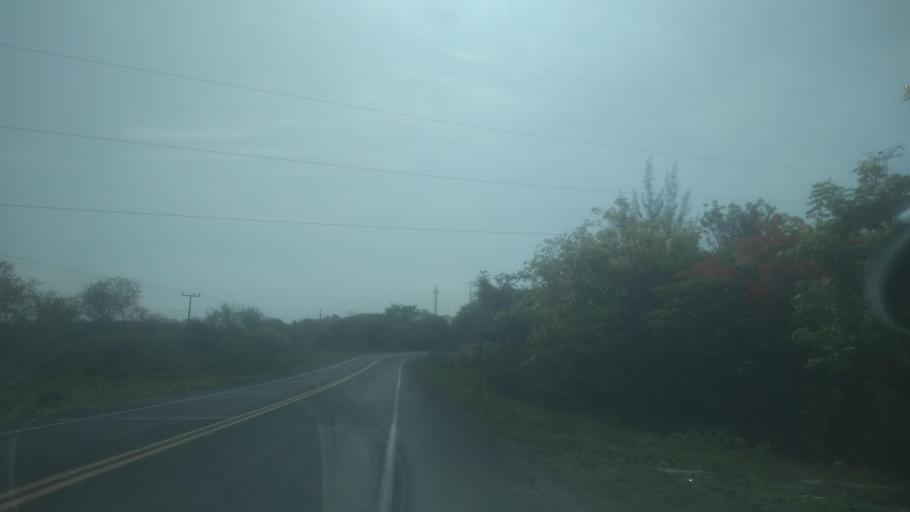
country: MX
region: Veracruz
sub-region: Emiliano Zapata
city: Plan del Rio
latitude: 19.3931
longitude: -96.6260
